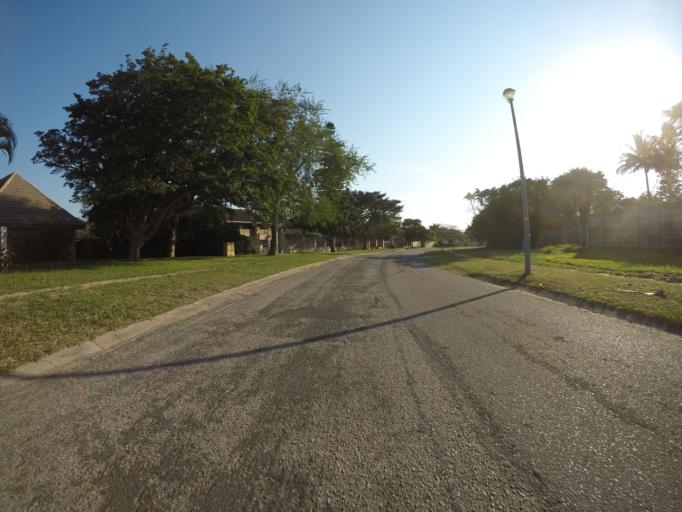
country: ZA
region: KwaZulu-Natal
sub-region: uThungulu District Municipality
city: Richards Bay
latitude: -28.7763
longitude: 32.1018
